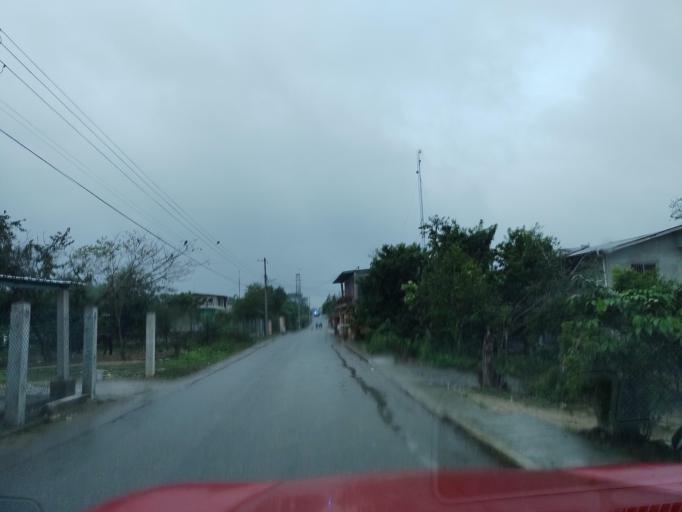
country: MX
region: Veracruz
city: Agua Dulce
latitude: 20.3372
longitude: -97.3146
